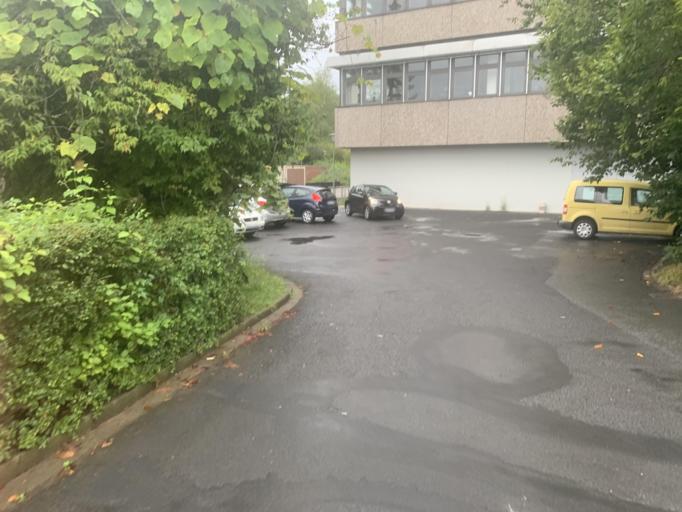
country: DE
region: Lower Saxony
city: Goettingen
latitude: 51.5582
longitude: 9.9523
